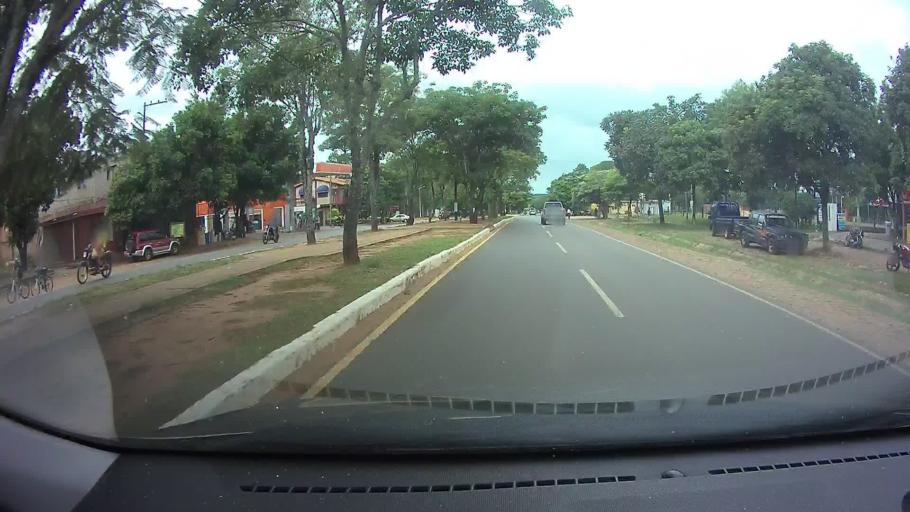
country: PY
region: Central
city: Nueva Italia
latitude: -25.6116
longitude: -57.4686
